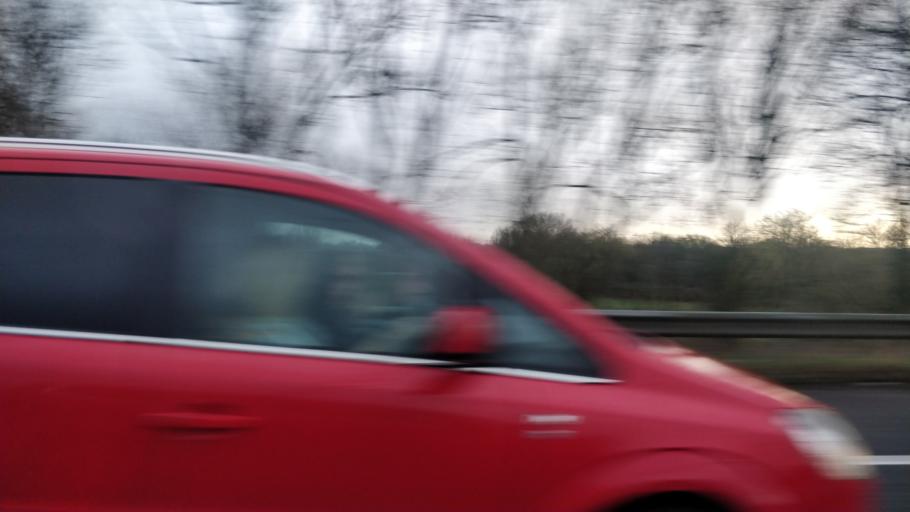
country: GB
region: England
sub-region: Knowsley
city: Kirkby
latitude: 53.4654
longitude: -2.8867
